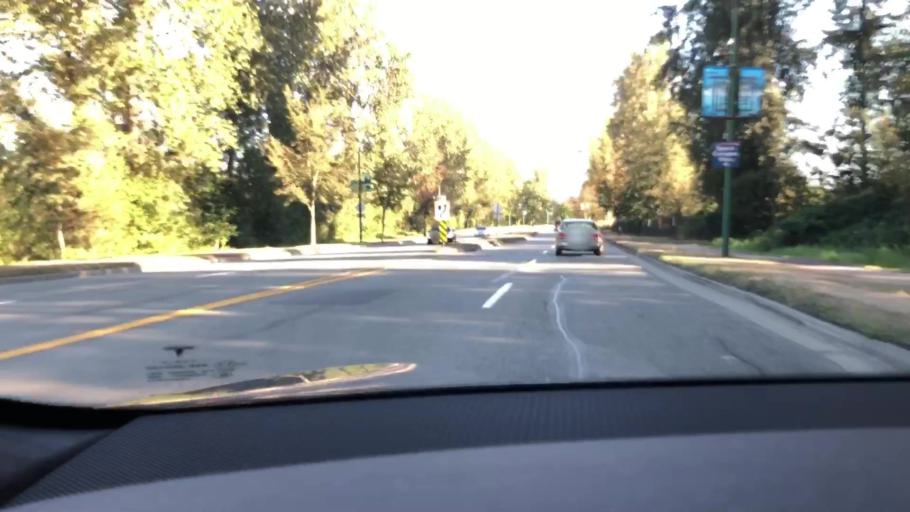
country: CA
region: British Columbia
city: Burnaby
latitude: 49.2578
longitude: -122.9683
